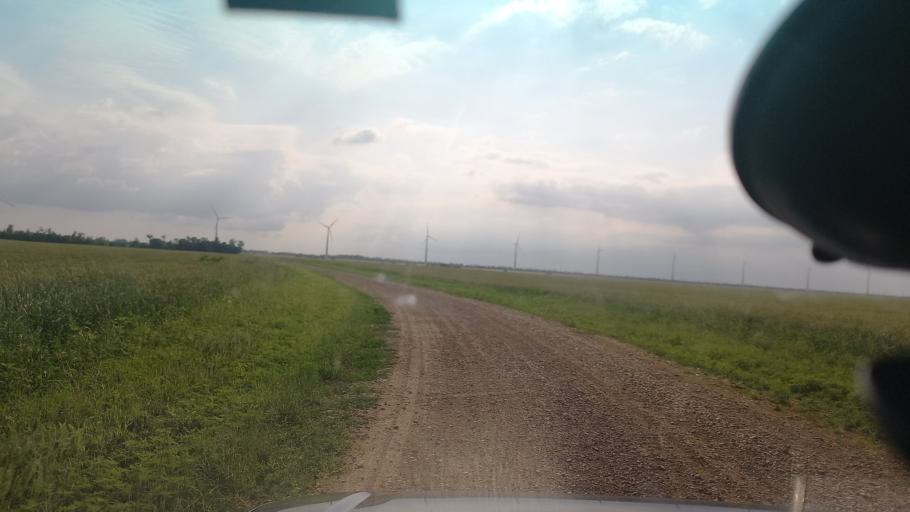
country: RU
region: Adygeya
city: Giaginskaya
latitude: 44.9556
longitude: 40.0996
